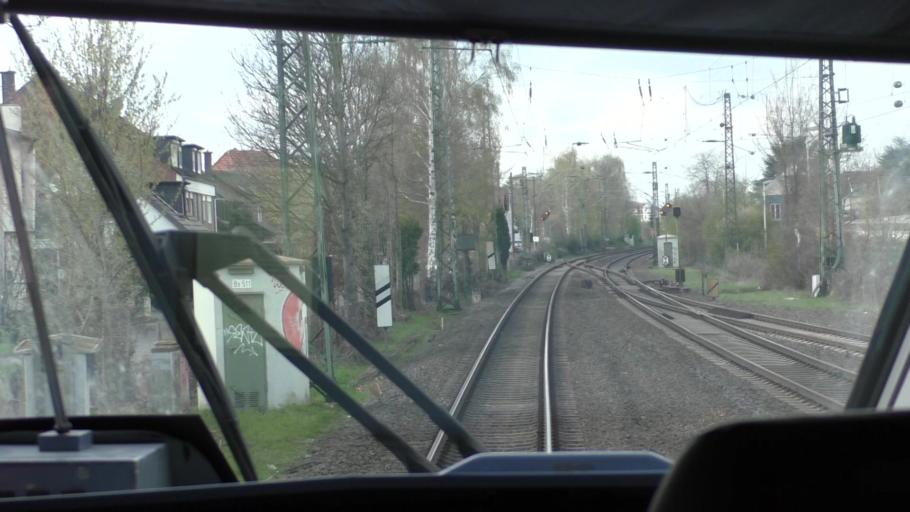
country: DE
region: North Rhine-Westphalia
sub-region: Regierungsbezirk Koln
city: Alfter
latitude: 50.7540
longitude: 7.0148
